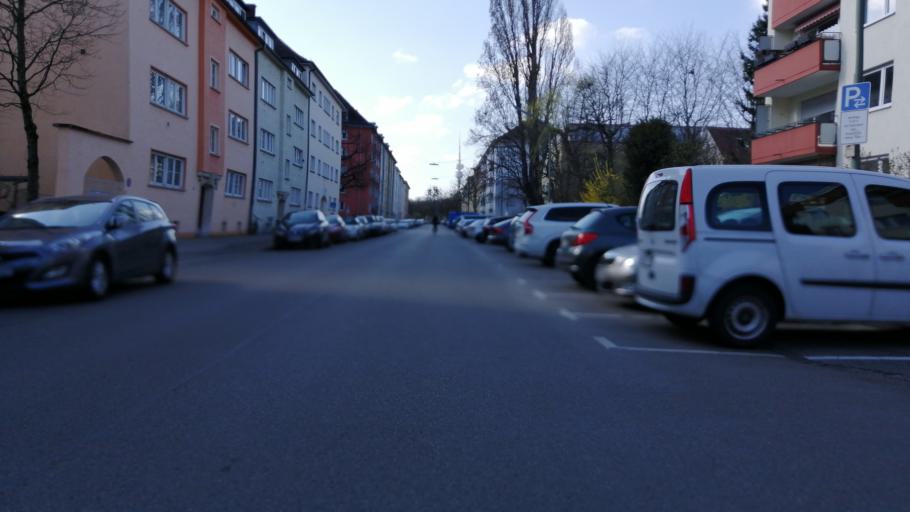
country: DE
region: Bavaria
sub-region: Upper Bavaria
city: Munich
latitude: 48.1691
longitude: 11.5823
